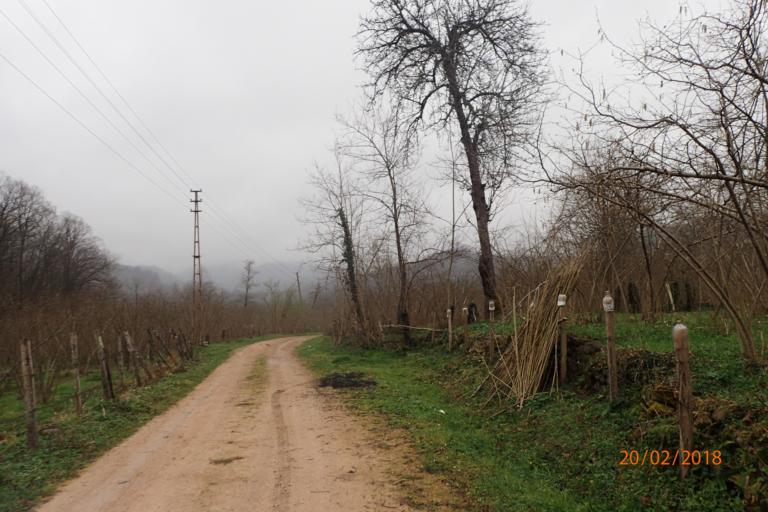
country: TR
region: Ordu
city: Camas
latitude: 40.9454
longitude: 37.5359
